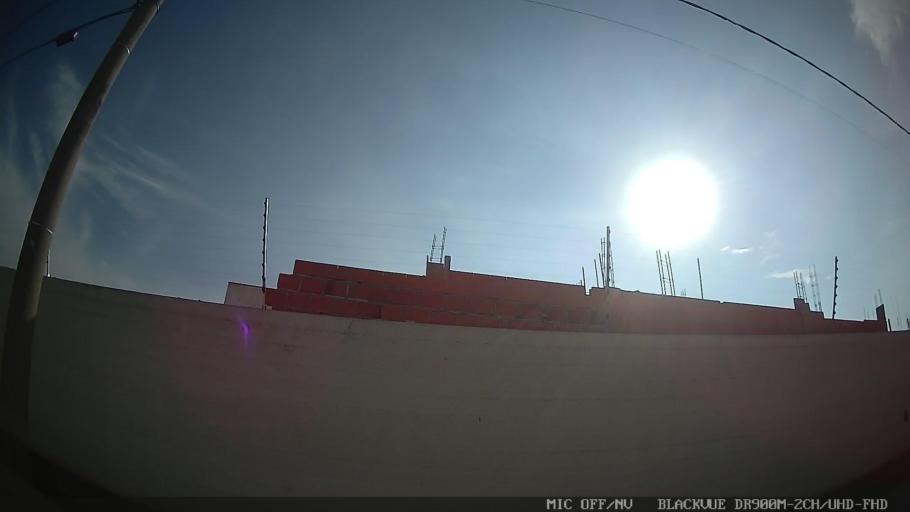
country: BR
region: Sao Paulo
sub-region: Indaiatuba
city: Indaiatuba
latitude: -23.0889
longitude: -47.2332
